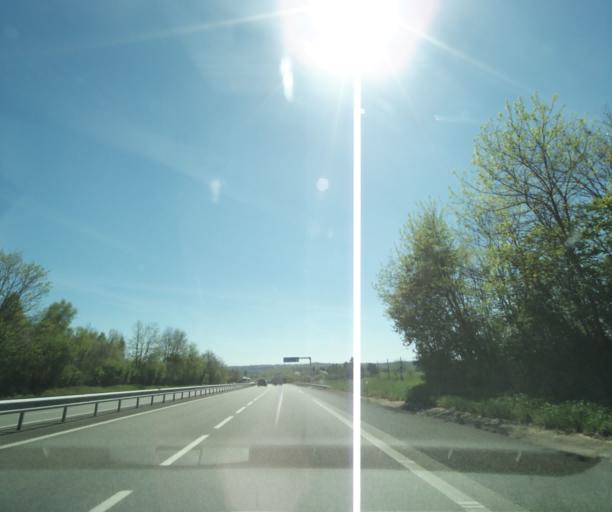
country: FR
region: Limousin
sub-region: Departement de la Correze
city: Vigeois
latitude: 45.3649
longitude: 1.5708
